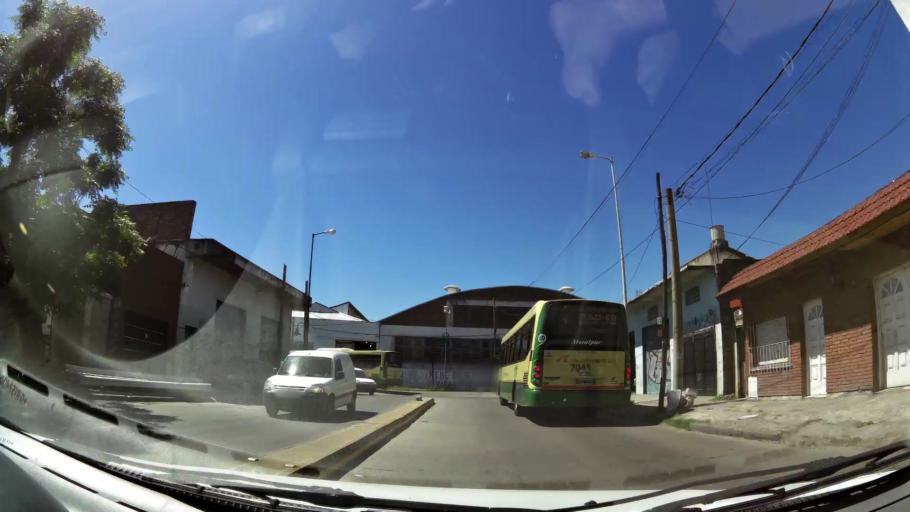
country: AR
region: Buenos Aires
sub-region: Partido de General San Martin
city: General San Martin
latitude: -34.5439
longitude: -58.5380
